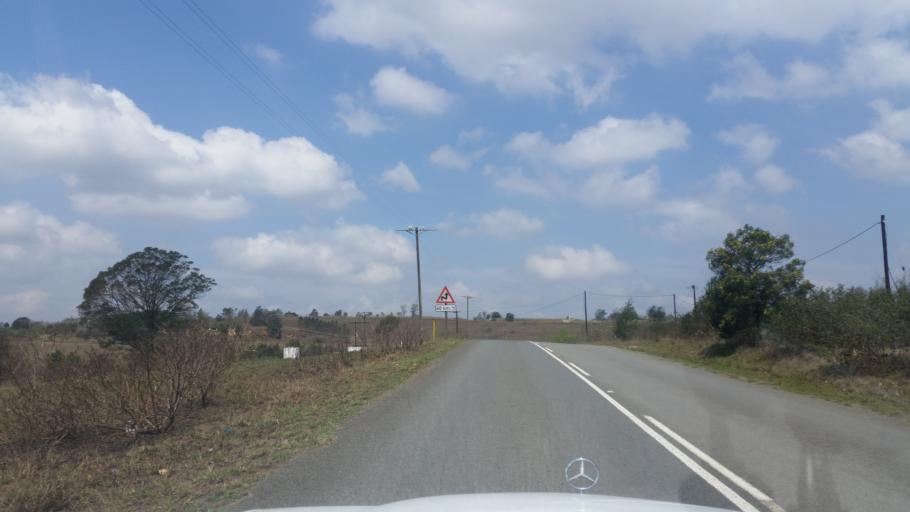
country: ZA
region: KwaZulu-Natal
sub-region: uMgungundlovu District Municipality
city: Camperdown
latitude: -29.7072
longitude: 30.4964
